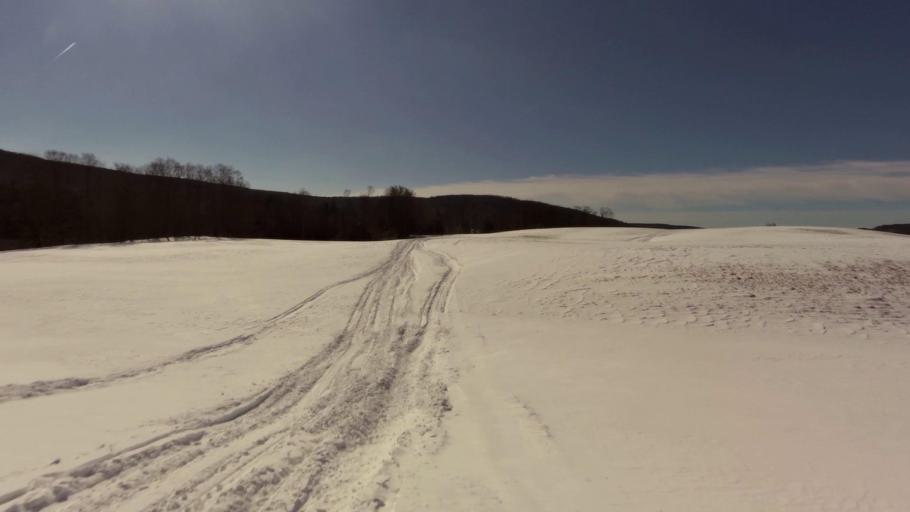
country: US
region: New York
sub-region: Allegany County
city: Cuba
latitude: 42.3396
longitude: -78.3055
